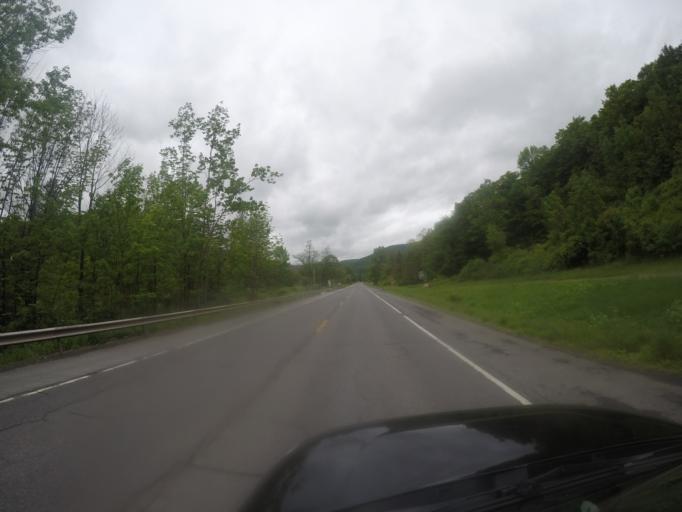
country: US
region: New York
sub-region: Ulster County
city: Shokan
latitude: 42.1181
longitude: -74.3808
